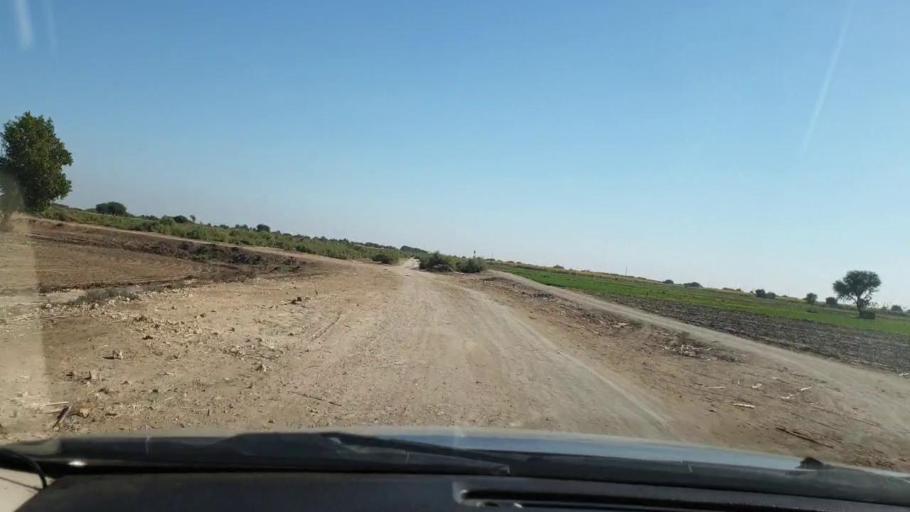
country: PK
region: Sindh
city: Berani
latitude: 25.7201
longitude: 68.9822
